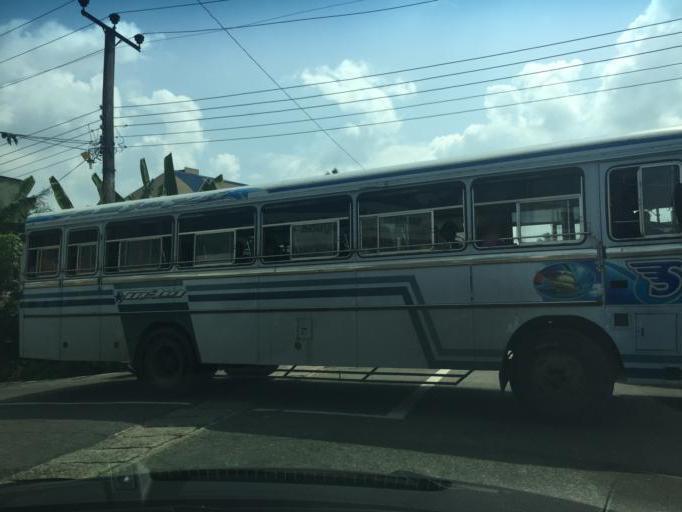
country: LK
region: Western
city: Horana South
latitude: 6.7182
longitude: 80.0586
